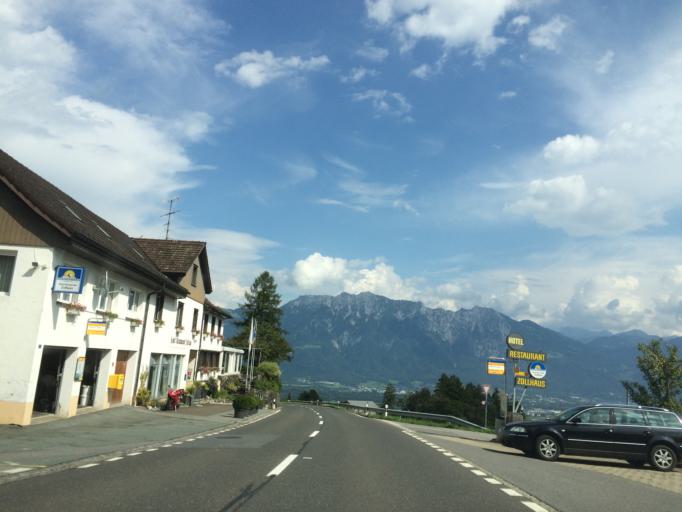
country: CH
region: Saint Gallen
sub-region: Wahlkreis Werdenberg
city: Gams
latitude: 47.1977
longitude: 9.4231
